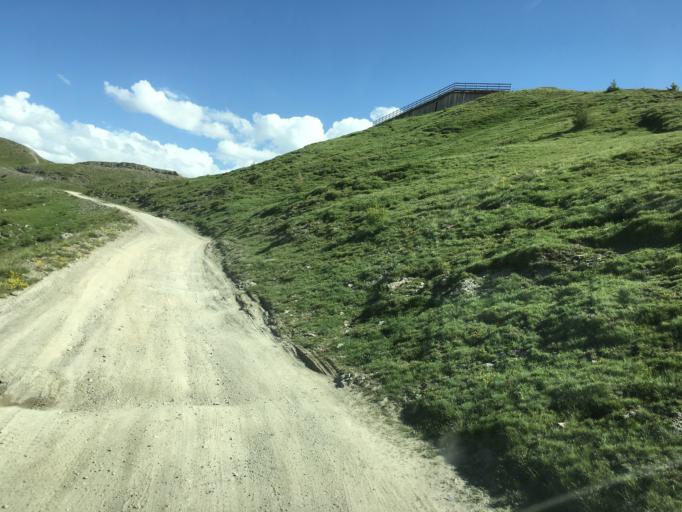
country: IT
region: Piedmont
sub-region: Provincia di Torino
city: Sestriere
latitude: 44.9877
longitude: 6.8687
